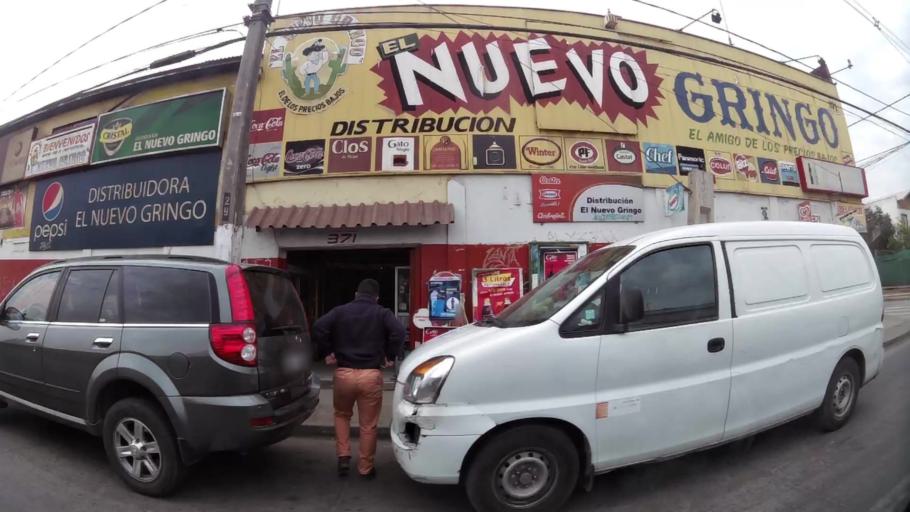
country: CL
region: Santiago Metropolitan
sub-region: Provincia de Chacabuco
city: Lampa
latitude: -33.2343
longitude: -70.8071
